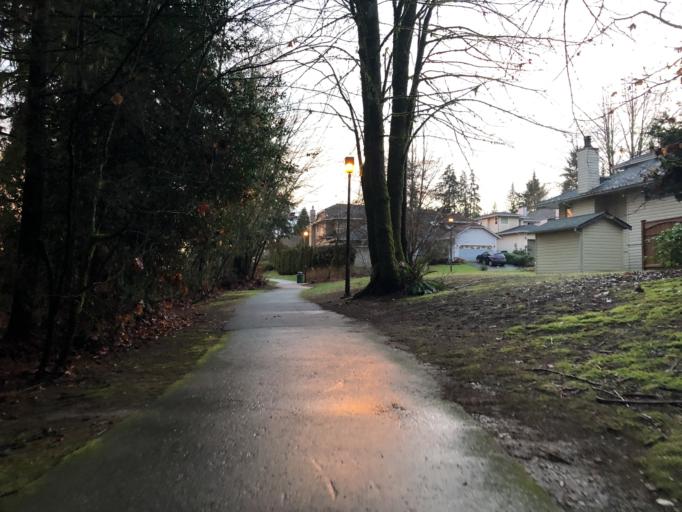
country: CA
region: British Columbia
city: Burnaby
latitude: 49.3208
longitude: -122.9586
